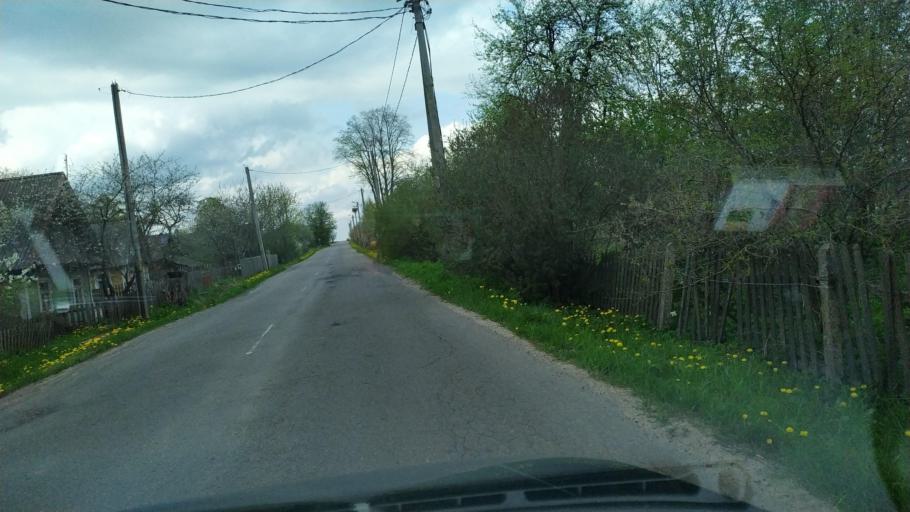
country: BY
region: Brest
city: Pruzhany
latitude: 52.6290
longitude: 24.3876
